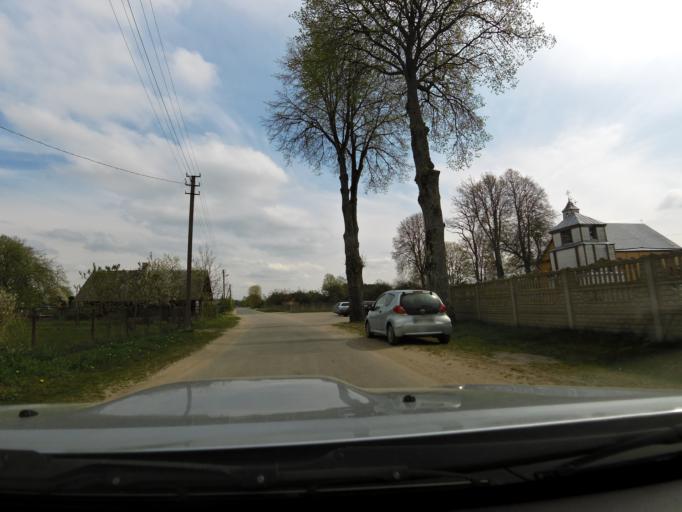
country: LT
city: Baltoji Voke
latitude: 54.4328
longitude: 25.1504
